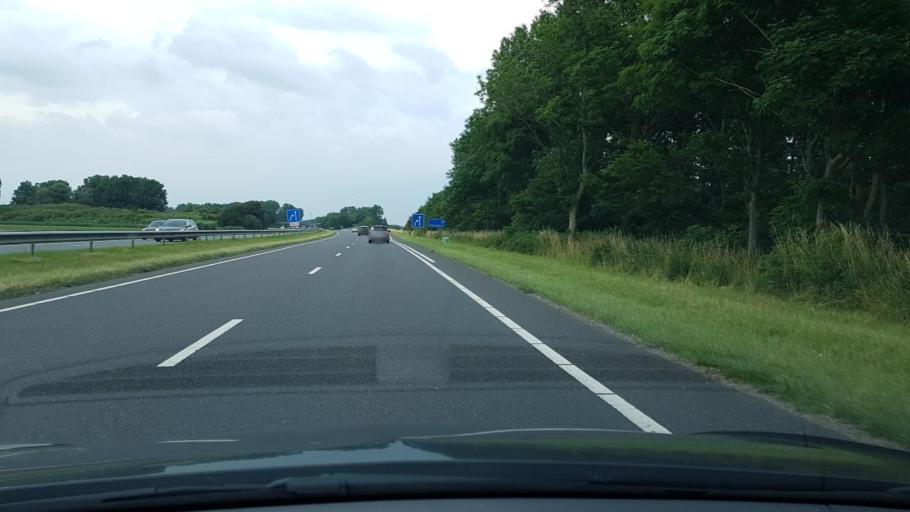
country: NL
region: South Holland
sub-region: Gemeente Noordwijk
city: Noordwijk-Binnen
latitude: 52.2159
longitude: 4.4484
